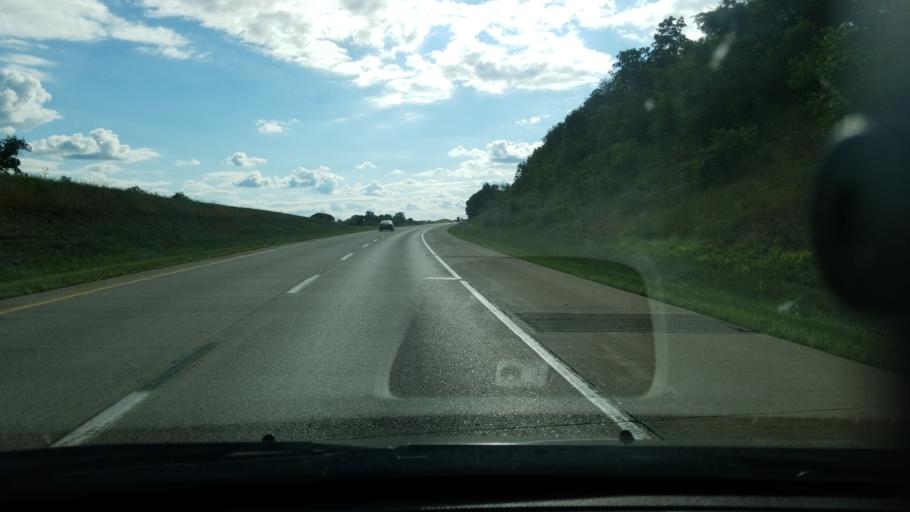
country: US
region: Pennsylvania
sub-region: Northumberland County
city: Riverside
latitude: 40.9902
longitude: -76.6629
